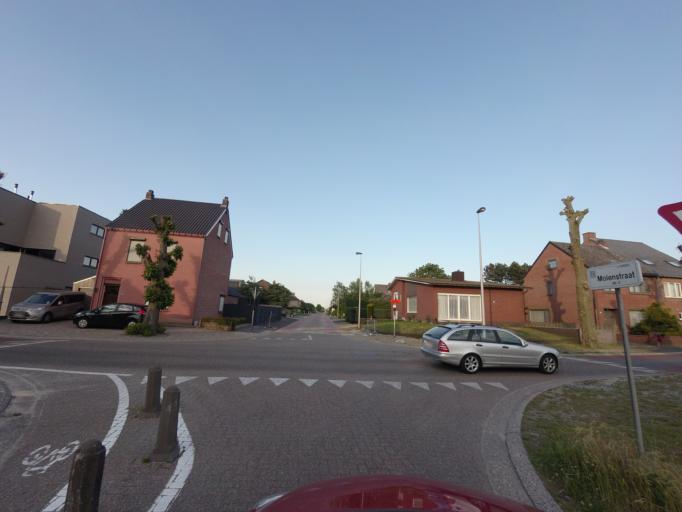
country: BE
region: Flanders
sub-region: Provincie Limburg
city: Lommel
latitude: 51.2325
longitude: 5.3162
